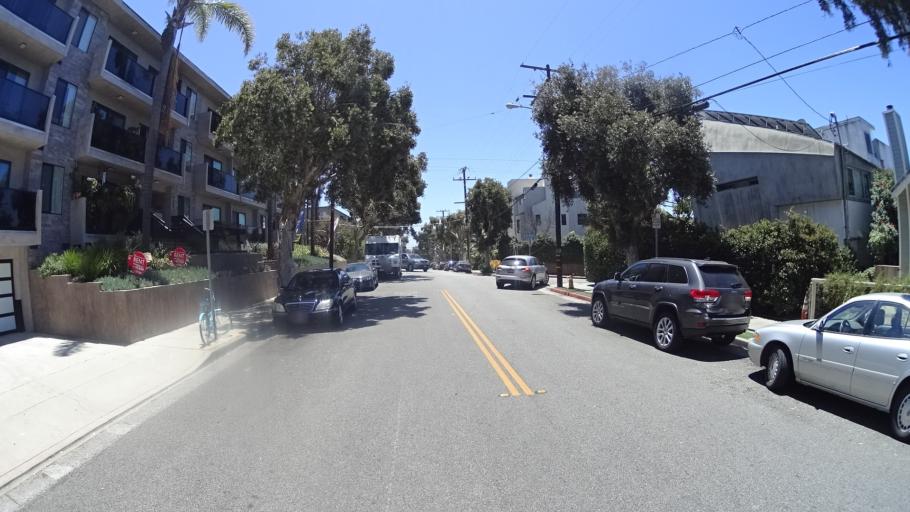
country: US
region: California
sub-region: Los Angeles County
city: Santa Monica
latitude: 34.0035
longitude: -118.4777
